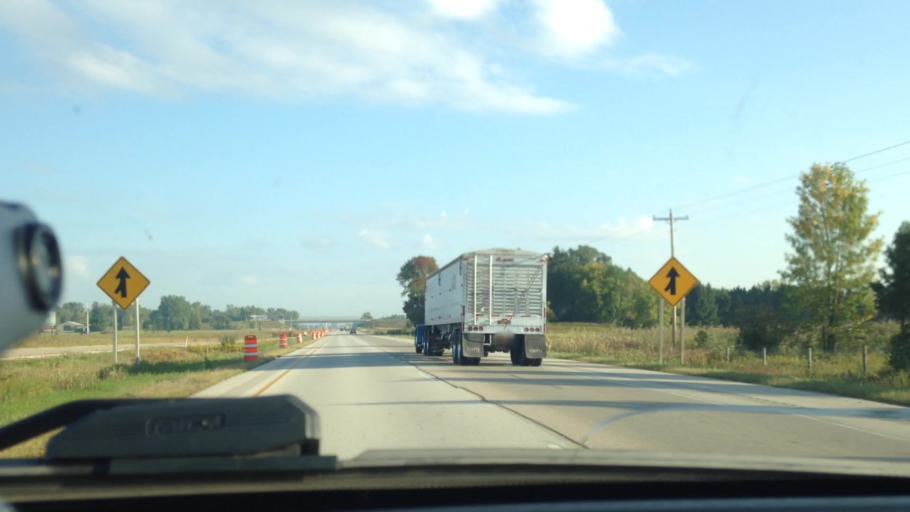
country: US
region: Wisconsin
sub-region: Brown County
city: Suamico
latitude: 44.7434
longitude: -88.0506
